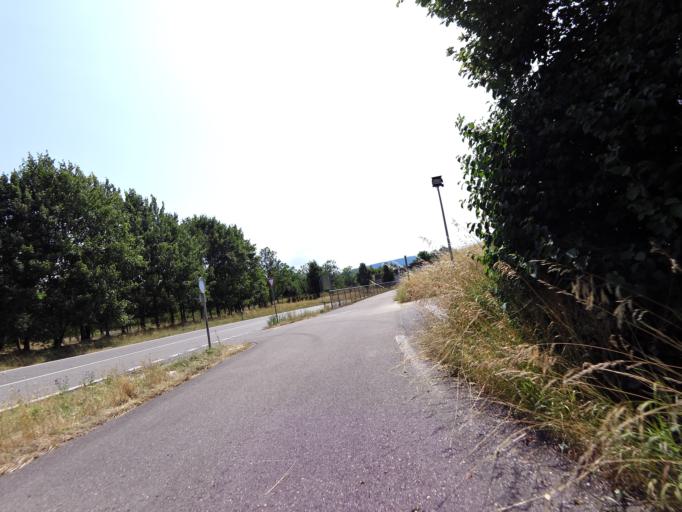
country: CH
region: Aargau
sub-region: Bezirk Baden
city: Birmenstorf
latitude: 47.4566
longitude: 8.2704
